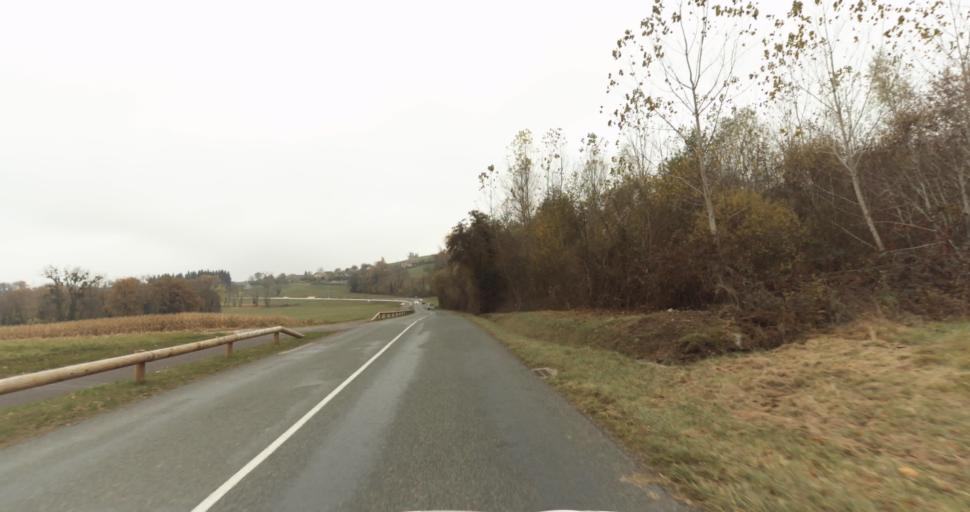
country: FR
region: Rhone-Alpes
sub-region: Departement de la Haute-Savoie
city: Alby-sur-Cheran
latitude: 45.8039
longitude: 6.0108
